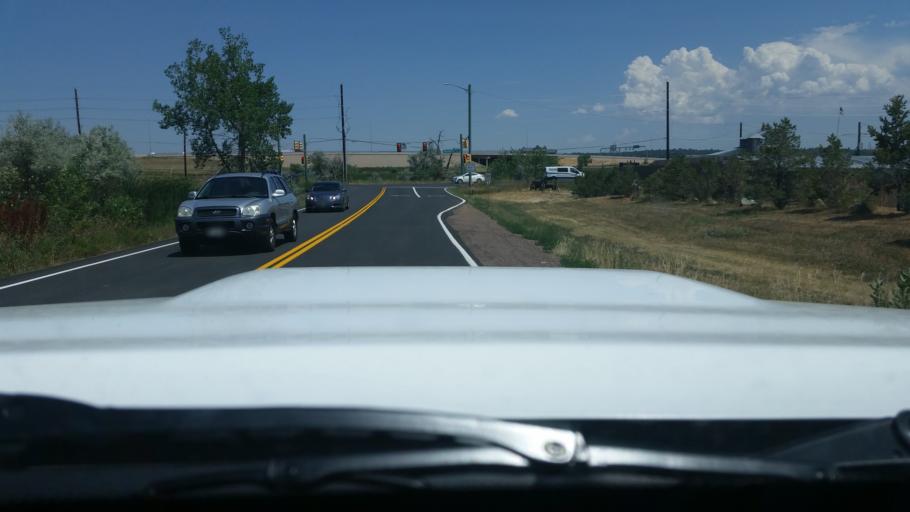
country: US
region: Colorado
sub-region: Broomfield County
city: Broomfield
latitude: 39.8925
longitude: -105.0826
